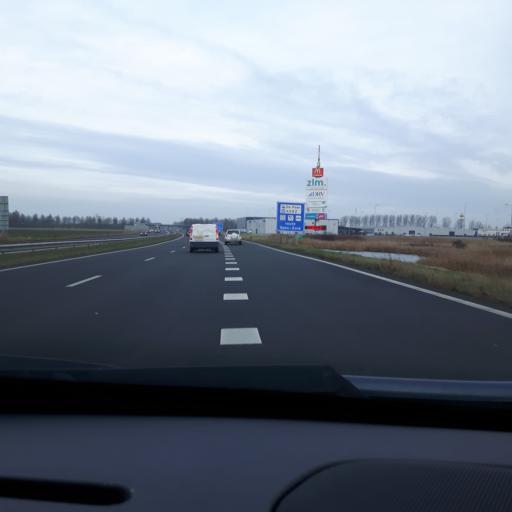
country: NL
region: Zeeland
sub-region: Gemeente Goes
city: Goes
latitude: 51.4870
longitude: 3.8713
